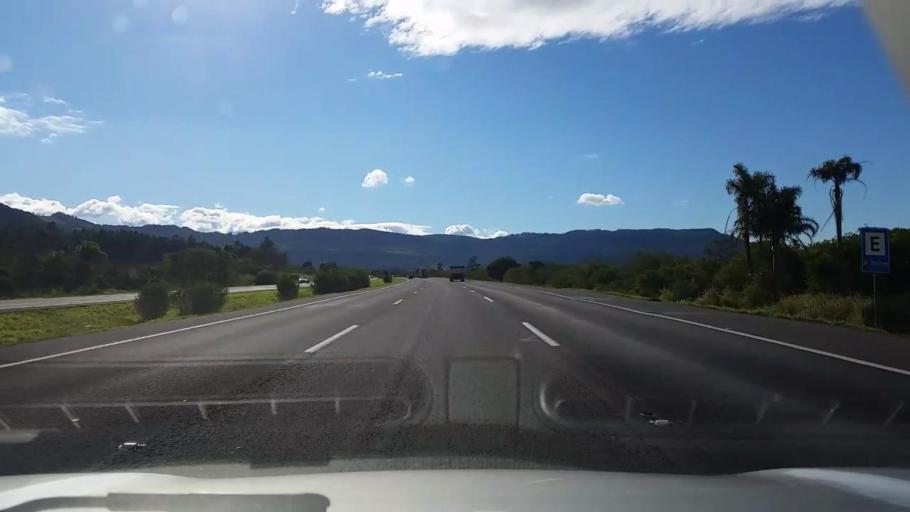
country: BR
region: Rio Grande do Sul
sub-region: Osorio
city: Osorio
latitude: -29.8818
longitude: -50.4362
